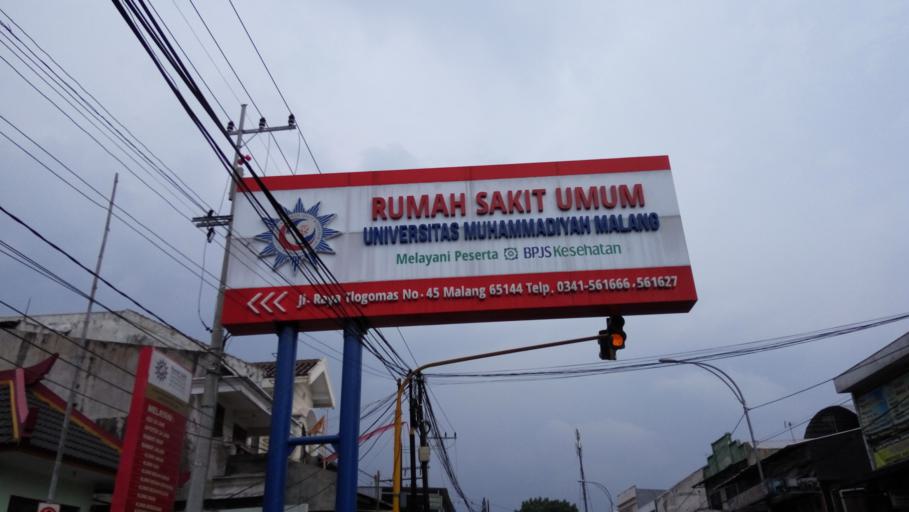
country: ID
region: East Java
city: Malang
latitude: -7.9248
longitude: 112.6001
